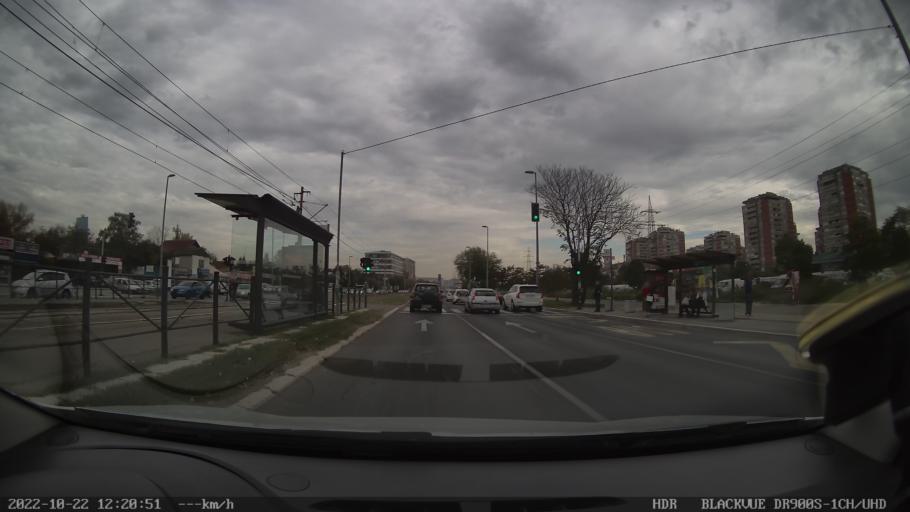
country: RS
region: Central Serbia
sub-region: Belgrade
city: Novi Beograd
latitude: 44.8036
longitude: 20.3956
